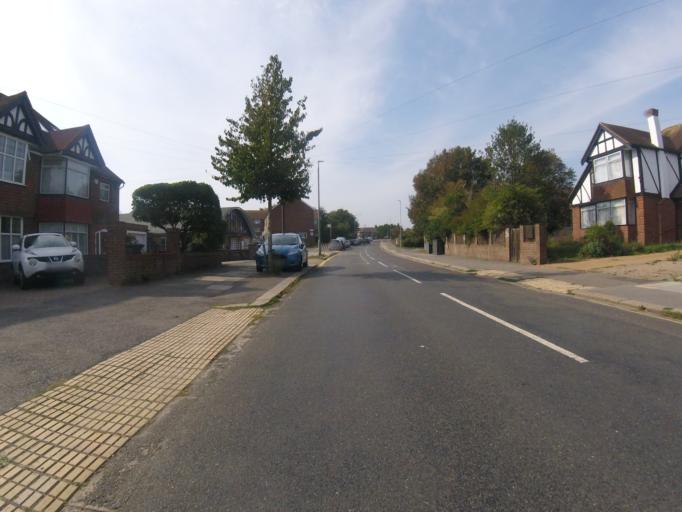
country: GB
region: England
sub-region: Brighton and Hove
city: Hove
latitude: 50.8467
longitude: -0.1829
